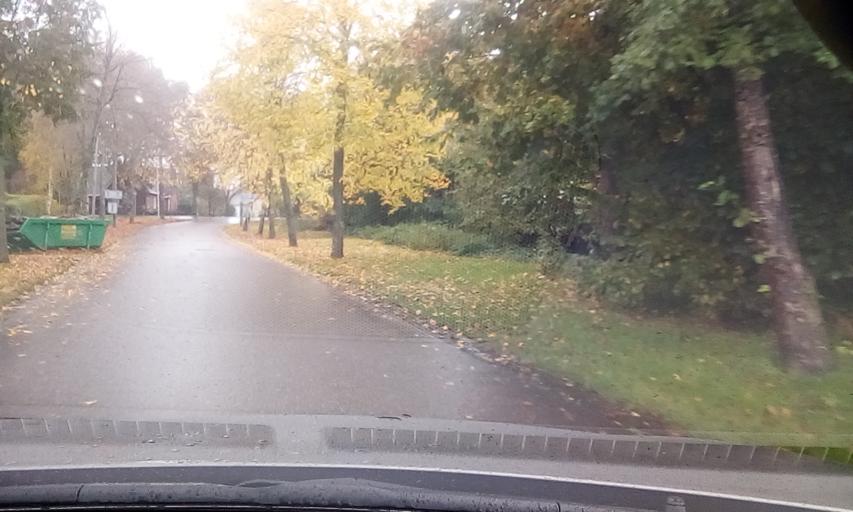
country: NL
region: Groningen
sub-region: Gemeente Hoogezand-Sappemeer
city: Hoogezand
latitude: 53.2075
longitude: 6.7054
